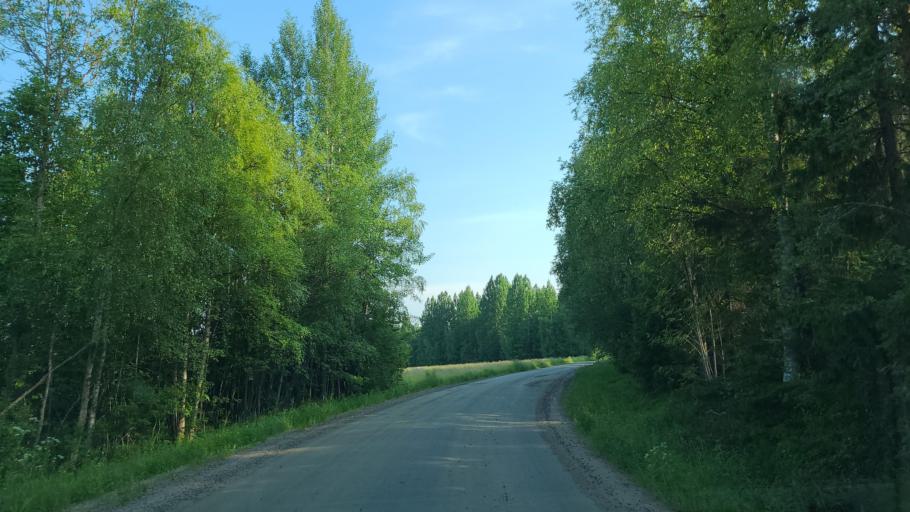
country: SE
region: Vaesterbotten
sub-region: Skelleftea Kommun
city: Burea
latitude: 64.4393
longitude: 21.5004
